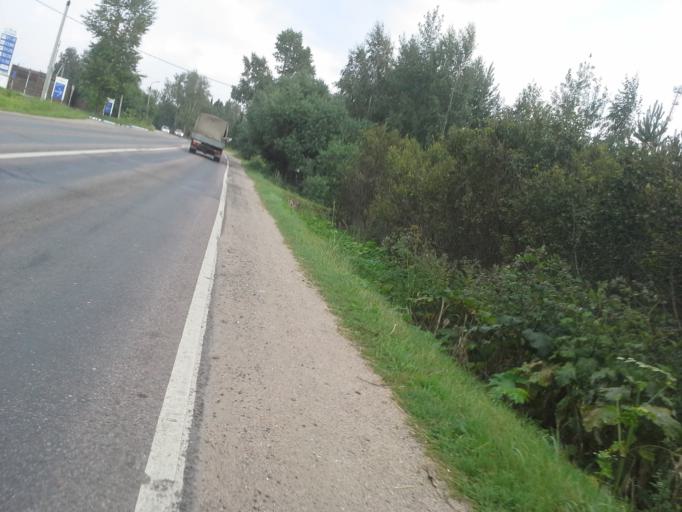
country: RU
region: Moskovskaya
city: Istra
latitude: 55.9306
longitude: 36.9354
